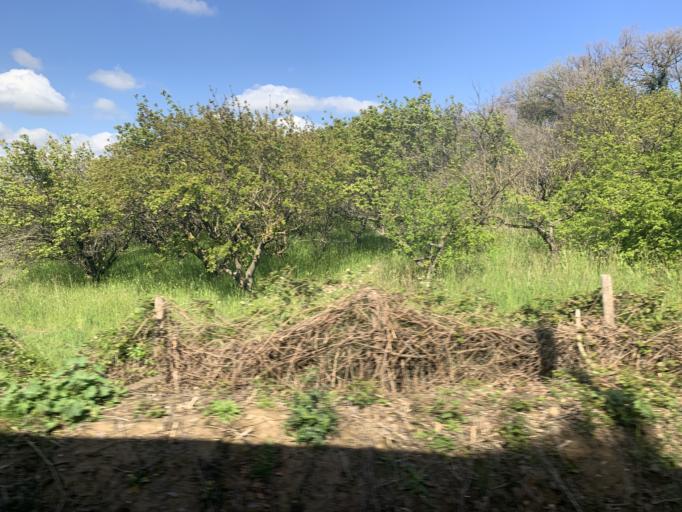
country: IT
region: Latium
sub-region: Citta metropolitana di Roma Capitale
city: Marino
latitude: 41.7792
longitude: 12.6428
